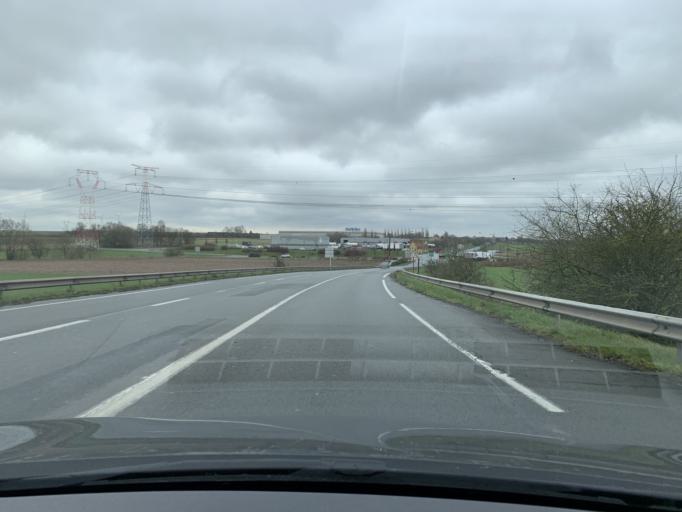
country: FR
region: Nord-Pas-de-Calais
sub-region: Departement du Nord
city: Hordain
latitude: 50.2521
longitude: 3.3221
